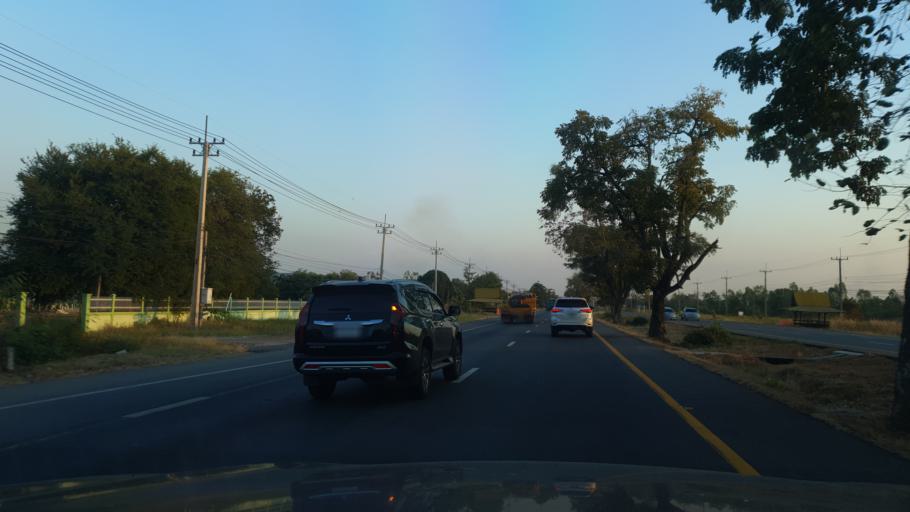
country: TH
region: Nakhon Sawan
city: Banphot Phisai
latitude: 15.8375
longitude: 99.9308
